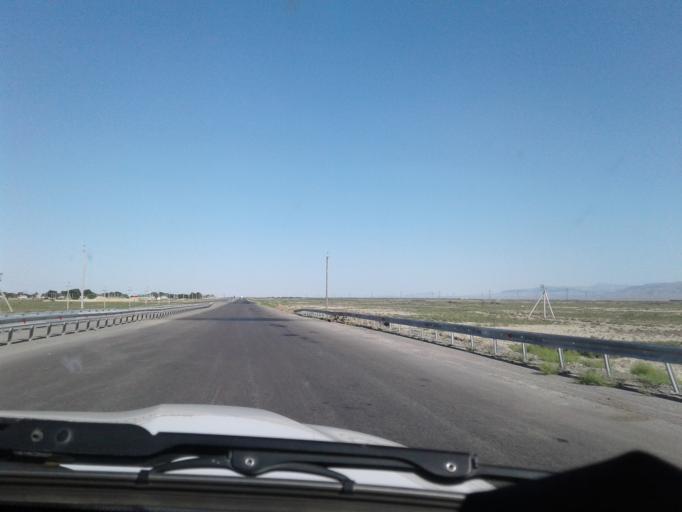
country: TM
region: Ahal
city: Kaka
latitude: 37.3105
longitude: 59.7560
